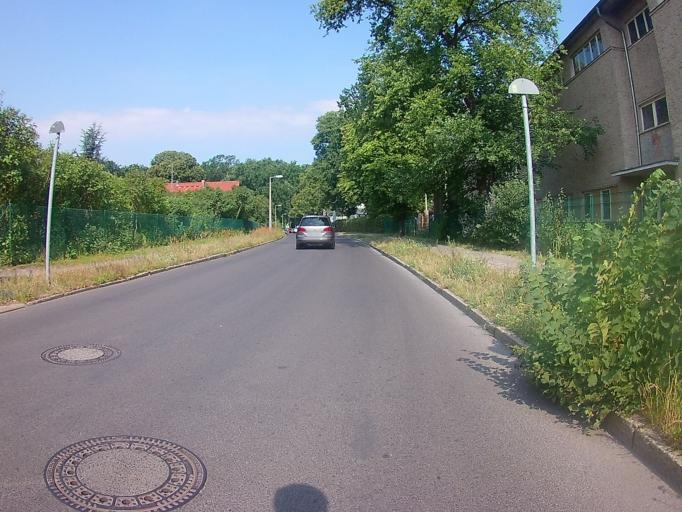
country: DE
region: Berlin
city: Grunau
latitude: 52.4120
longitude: 13.5872
